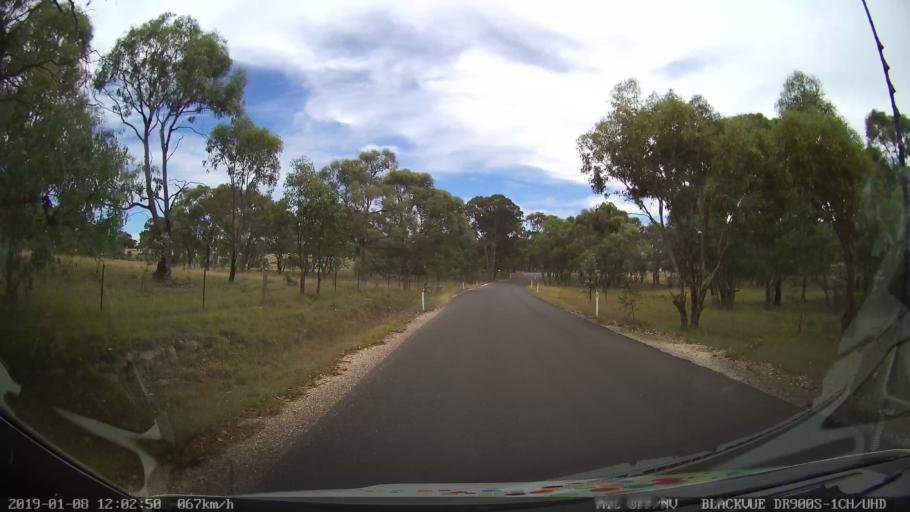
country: AU
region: New South Wales
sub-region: Armidale Dumaresq
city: Armidale
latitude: -30.4530
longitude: 151.6001
